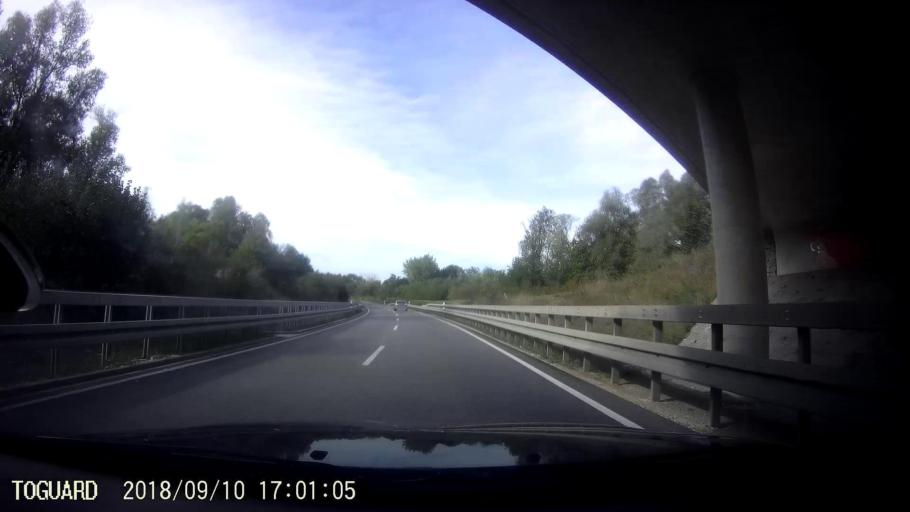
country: CH
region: Thurgau
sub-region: Kreuzlingen District
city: Gottlieben
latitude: 47.6911
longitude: 9.1369
